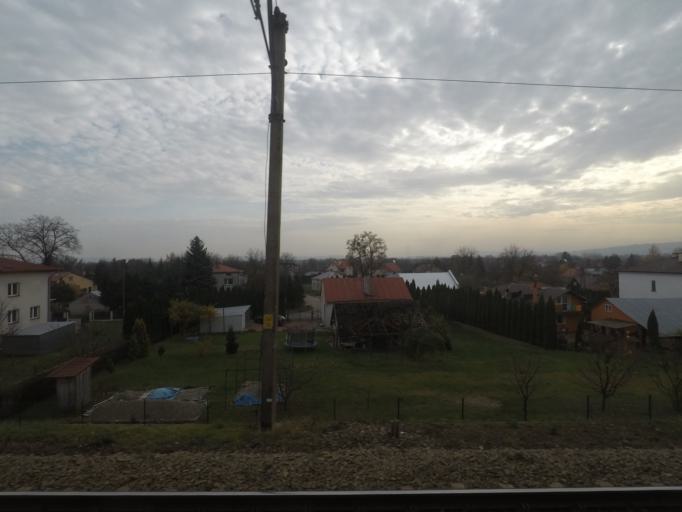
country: PL
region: Subcarpathian Voivodeship
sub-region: Powiat przemyski
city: Zurawica
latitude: 49.8033
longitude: 22.8030
